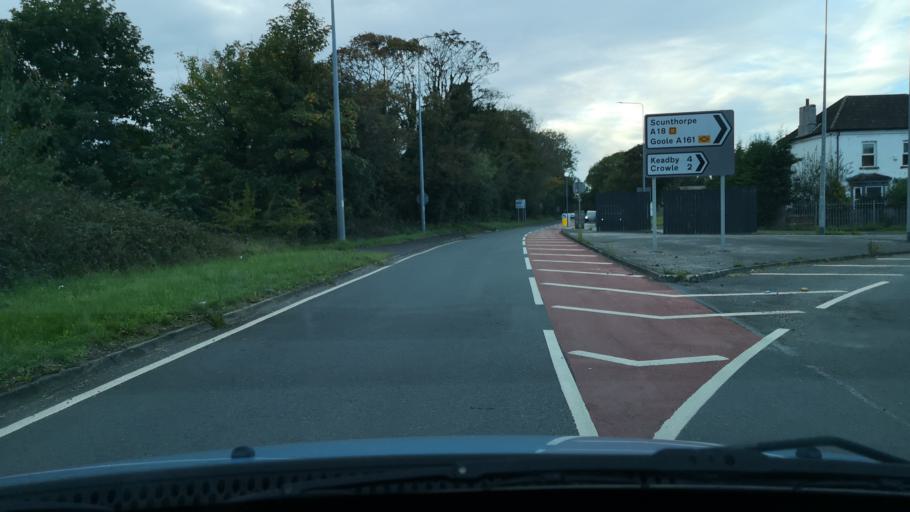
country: GB
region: England
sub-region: North Lincolnshire
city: Crowle
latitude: 53.5858
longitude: -0.8193
